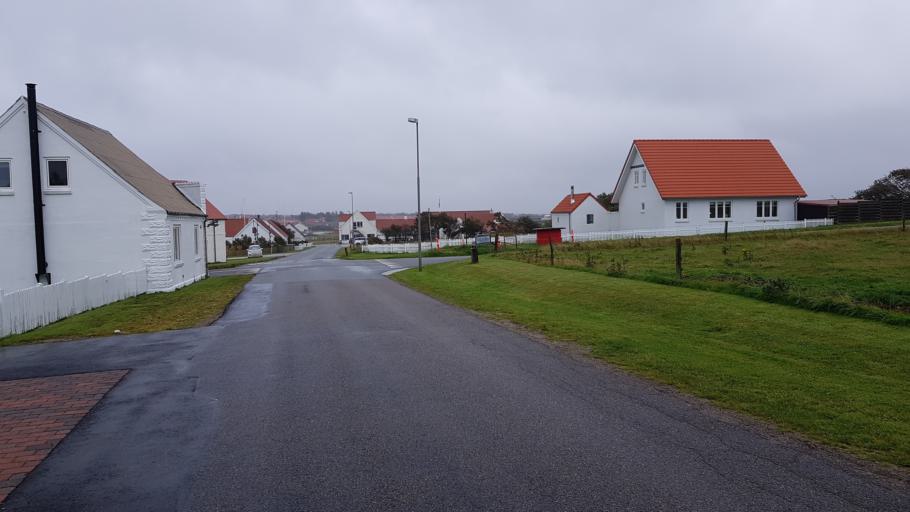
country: DK
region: North Denmark
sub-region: Thisted Kommune
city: Hanstholm
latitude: 57.1153
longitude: 8.5996
